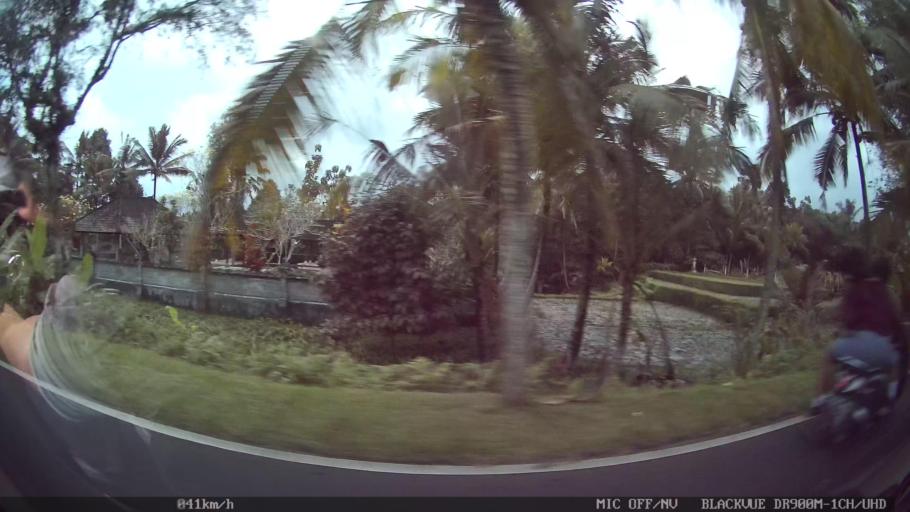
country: ID
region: Bali
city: Pohgending Kangin
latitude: -8.4322
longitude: 115.1433
